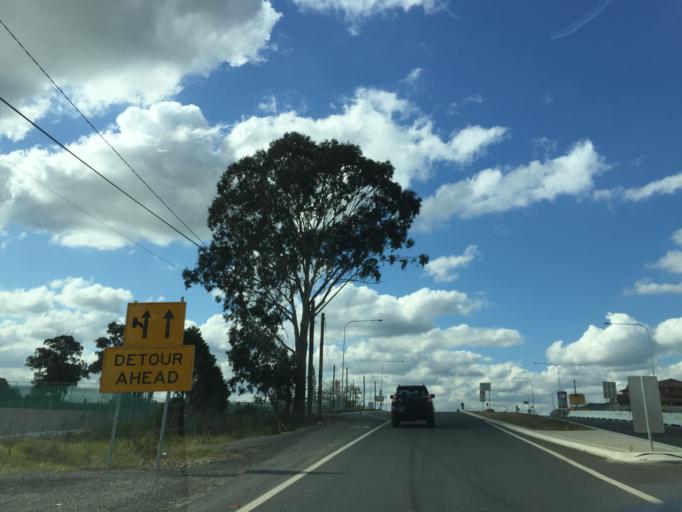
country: AU
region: New South Wales
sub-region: Blacktown
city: Rouse Hill
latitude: -33.6955
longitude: 150.9009
